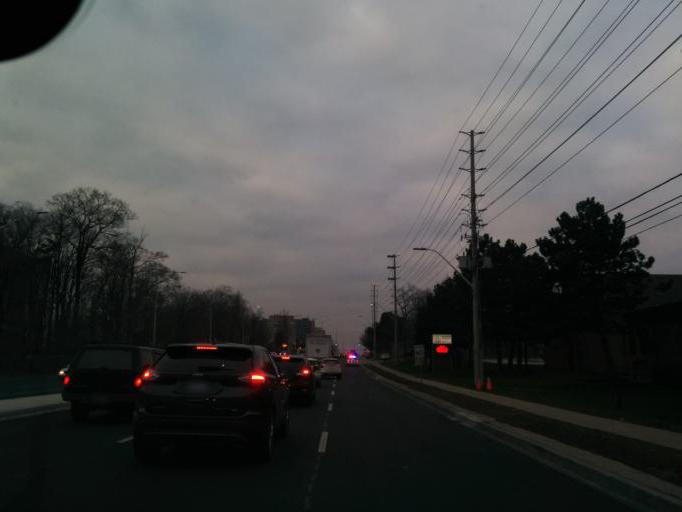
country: CA
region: Ontario
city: Etobicoke
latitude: 43.6199
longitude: -79.5988
